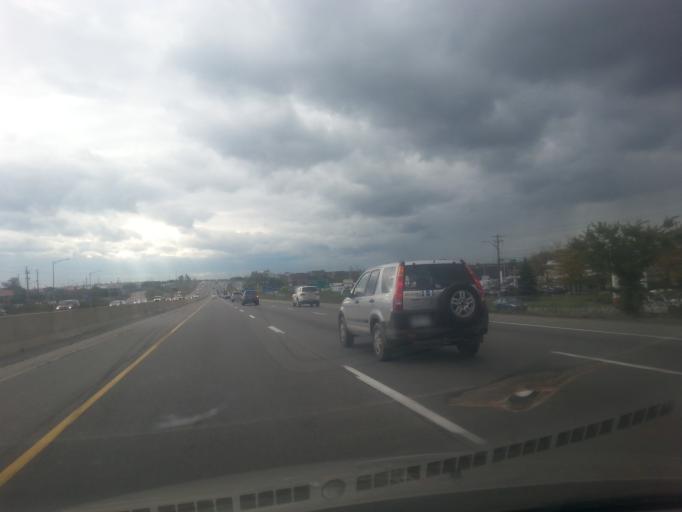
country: CA
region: Ontario
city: Oshawa
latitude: 43.8729
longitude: -78.8890
